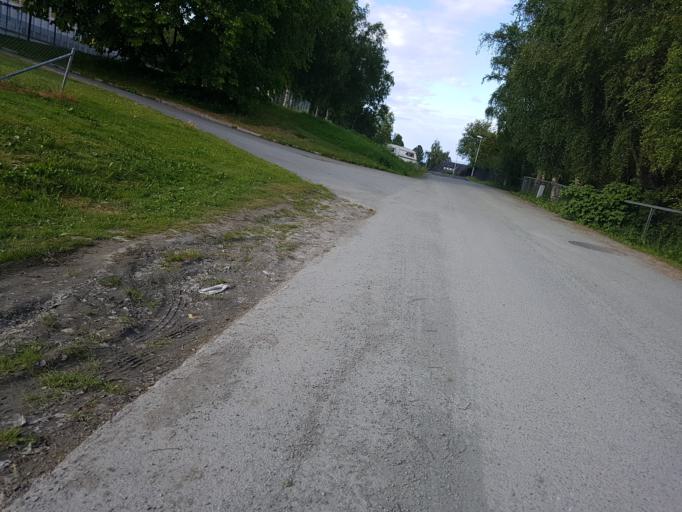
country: NO
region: Sor-Trondelag
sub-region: Trondheim
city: Trondheim
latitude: 63.4175
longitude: 10.3667
